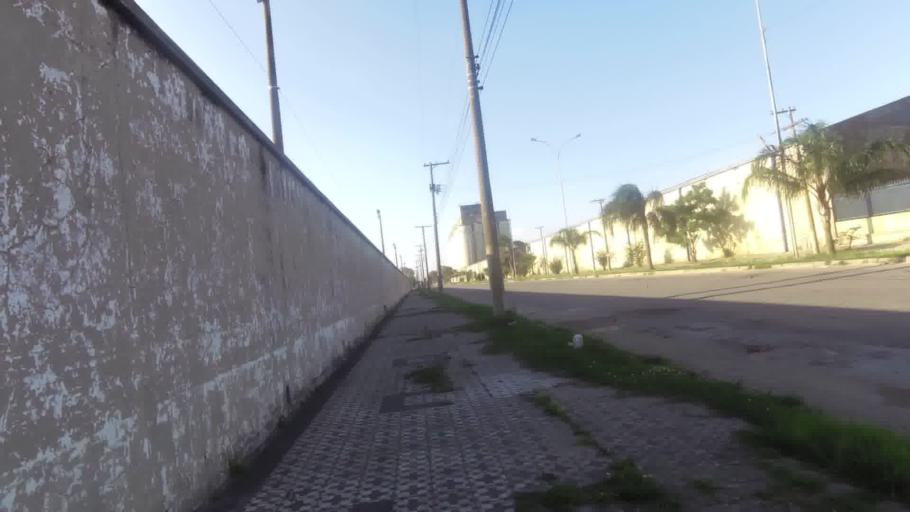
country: BR
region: Rio Grande do Sul
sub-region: Rio Grande
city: Rio Grande
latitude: -32.0385
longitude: -52.0780
